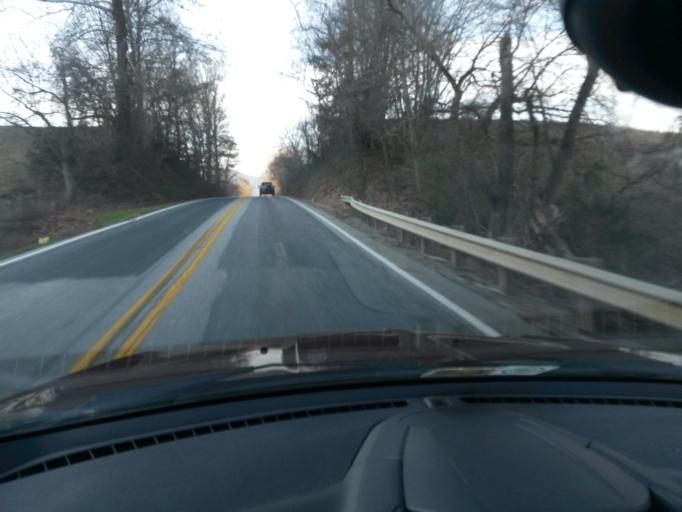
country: US
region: Virginia
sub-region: Amherst County
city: Amherst
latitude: 37.6515
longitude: -79.1345
